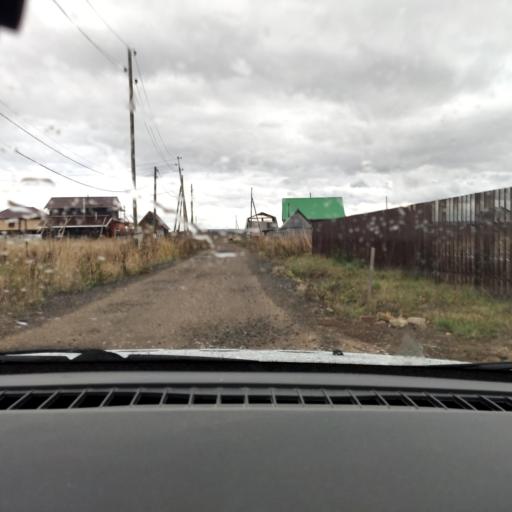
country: RU
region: Perm
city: Kultayevo
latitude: 57.8965
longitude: 55.9574
